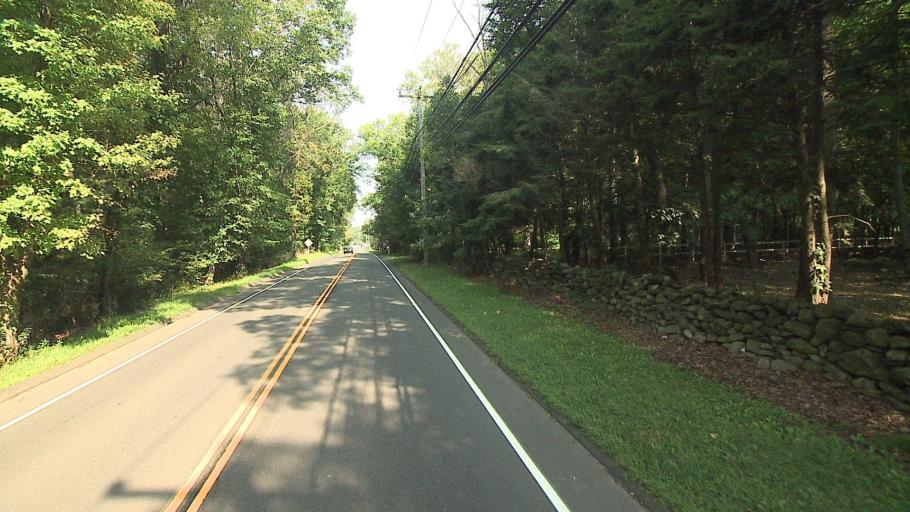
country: US
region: Connecticut
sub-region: Fairfield County
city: Wilton
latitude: 41.1985
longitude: -73.3788
